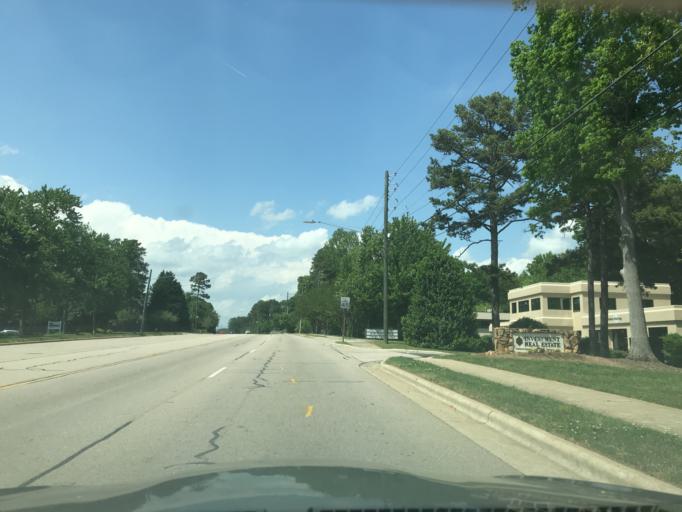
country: US
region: North Carolina
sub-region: Wake County
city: West Raleigh
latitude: 35.8849
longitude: -78.6464
